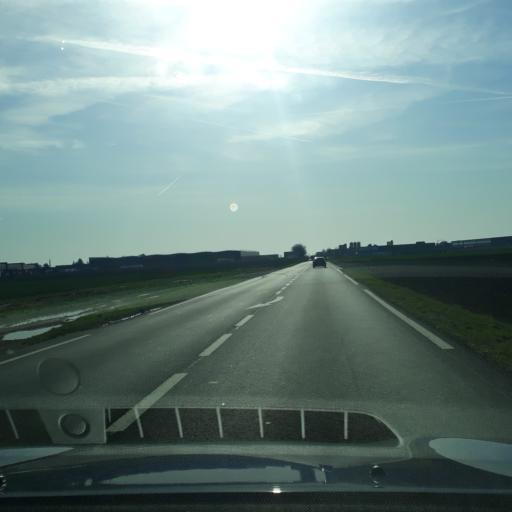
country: FR
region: Ile-de-France
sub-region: Departement de l'Essonne
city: Corbreuse
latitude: 48.4552
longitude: 1.9155
